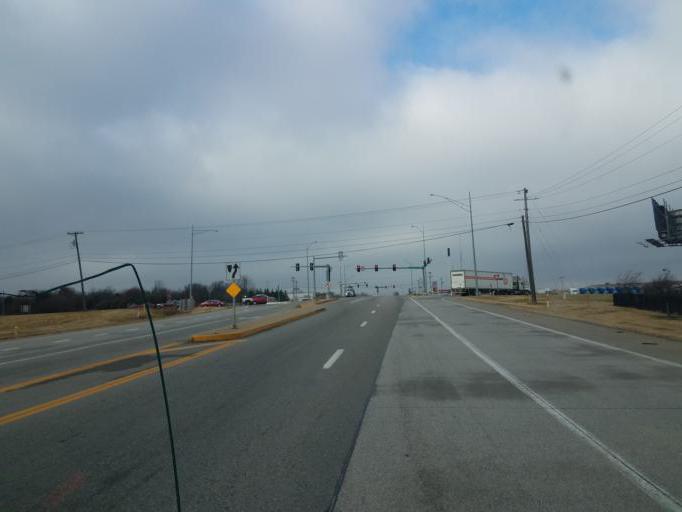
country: US
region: Missouri
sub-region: Greene County
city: Springfield
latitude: 37.2389
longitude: -93.2229
